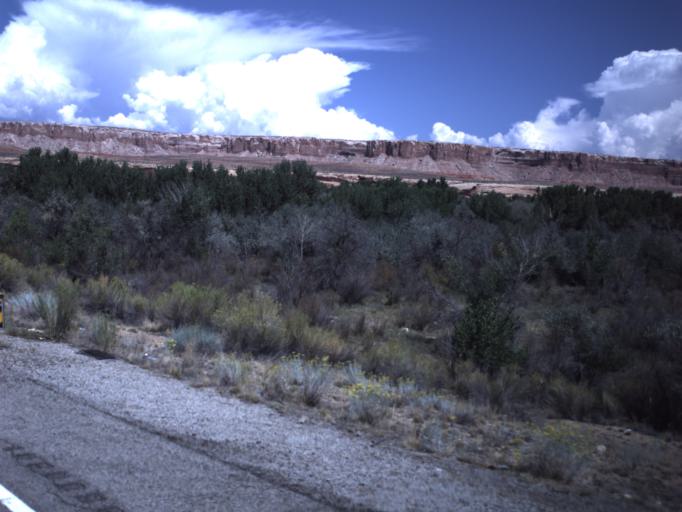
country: US
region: Utah
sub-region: San Juan County
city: Blanding
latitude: 37.2561
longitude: -109.6170
